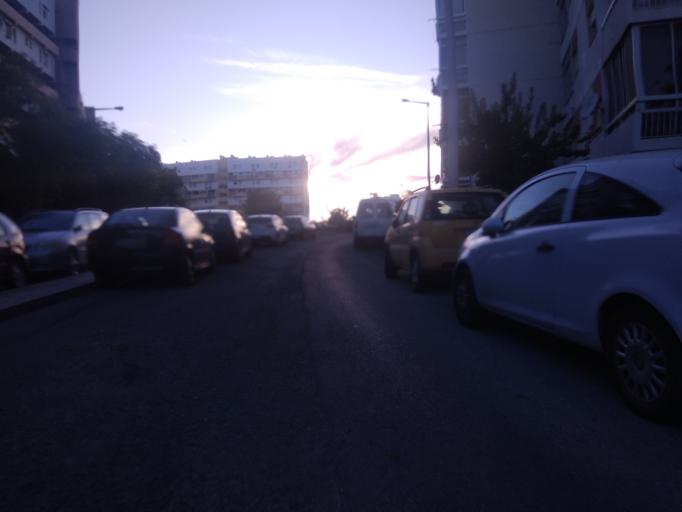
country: PT
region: Faro
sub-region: Faro
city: Faro
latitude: 37.0219
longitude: -7.9296
